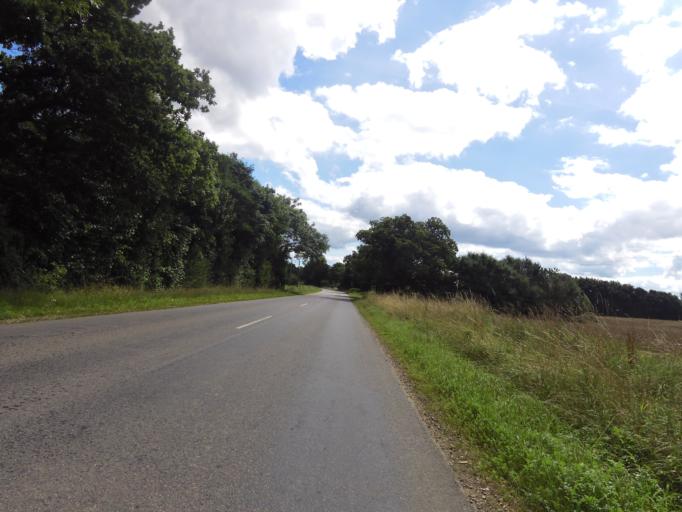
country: DK
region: South Denmark
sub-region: Haderslev Kommune
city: Haderslev
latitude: 55.2810
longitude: 9.4071
